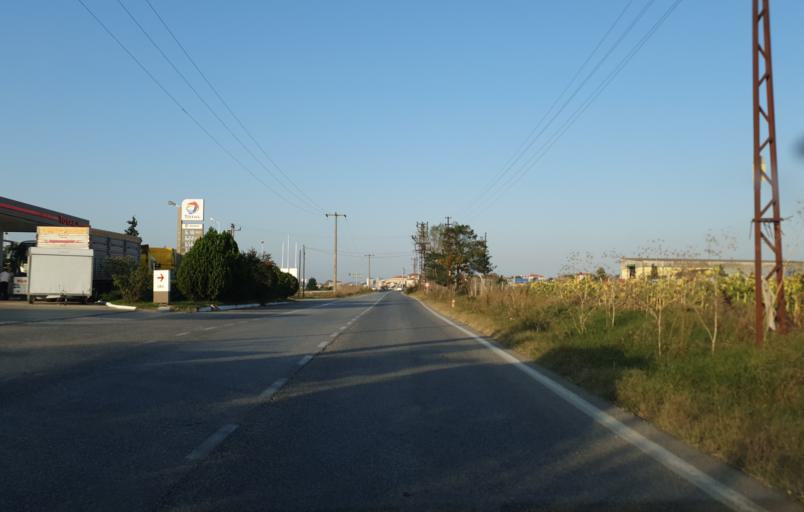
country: TR
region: Tekirdag
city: Saray
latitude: 41.4366
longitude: 27.9016
